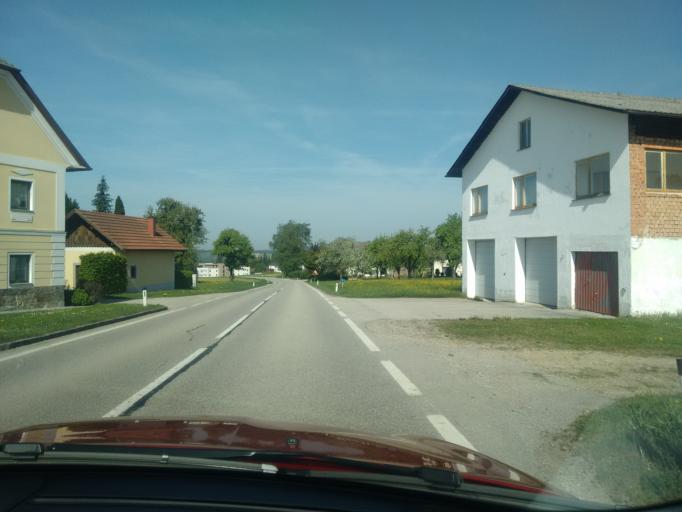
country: AT
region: Upper Austria
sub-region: Politischer Bezirk Grieskirchen
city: Grieskirchen
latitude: 48.3446
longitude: 13.7879
